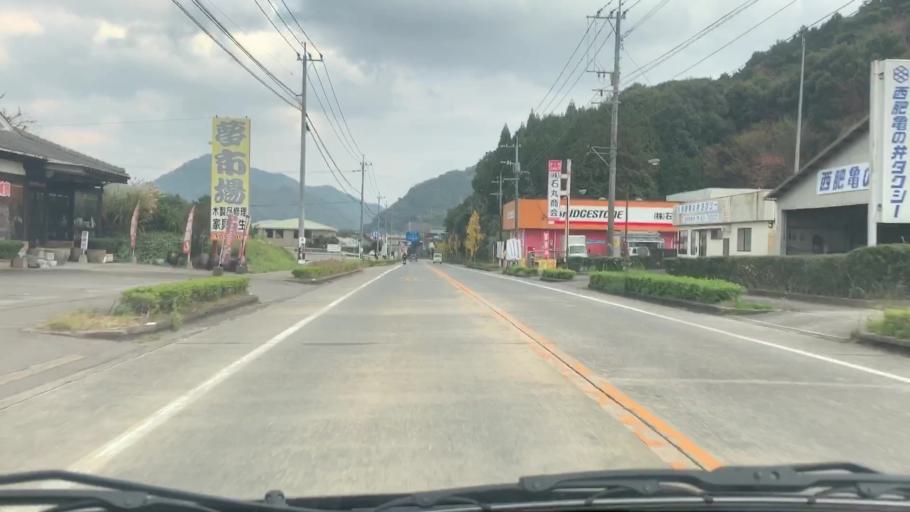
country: JP
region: Saga Prefecture
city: Imaricho-ko
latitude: 33.1836
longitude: 129.8736
